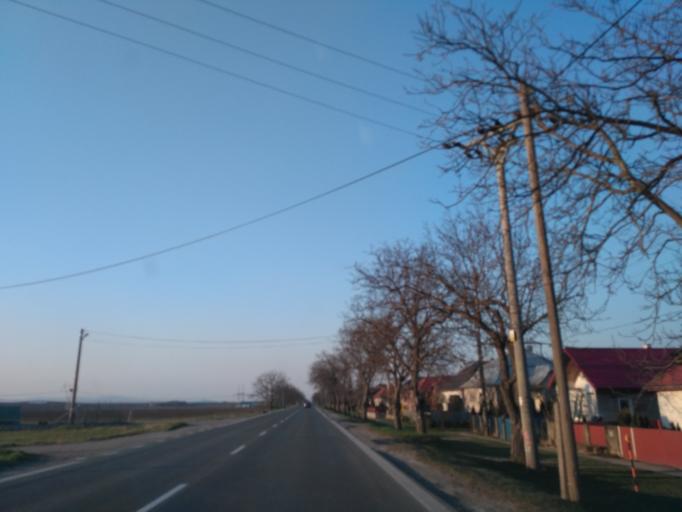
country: HU
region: Borsod-Abauj-Zemplen
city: Gonc
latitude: 48.5681
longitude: 21.2570
